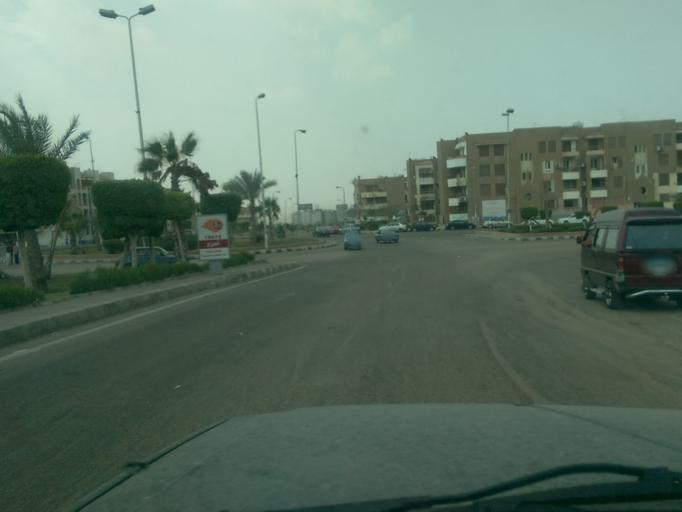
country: EG
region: Muhafazat al Qahirah
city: Halwan
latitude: 29.9858
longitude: 31.4303
